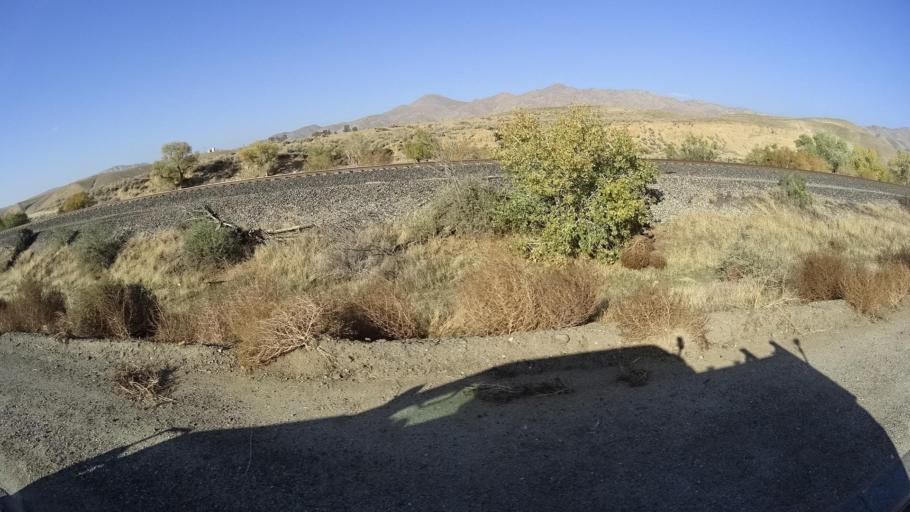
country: US
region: California
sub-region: Kern County
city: Arvin
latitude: 35.3253
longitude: -118.7310
